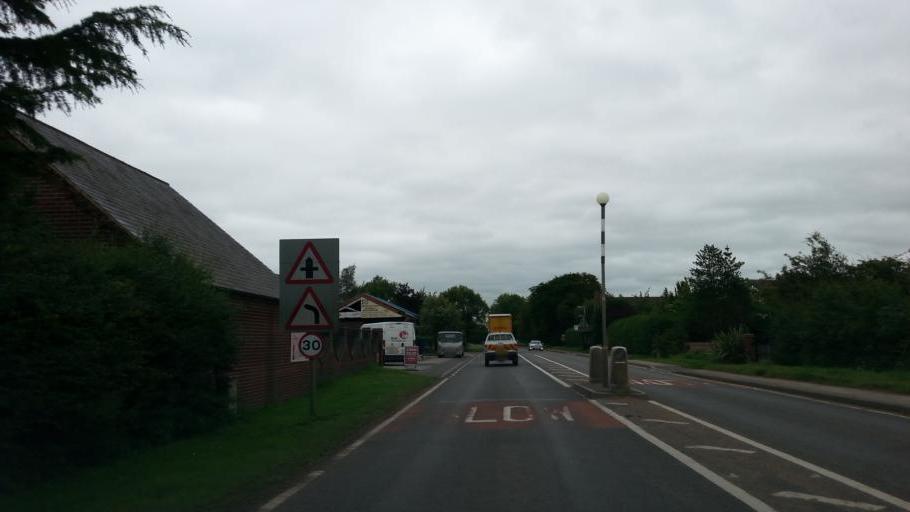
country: GB
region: England
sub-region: Nottinghamshire
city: Newark on Trent
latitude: 53.1064
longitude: -0.8222
